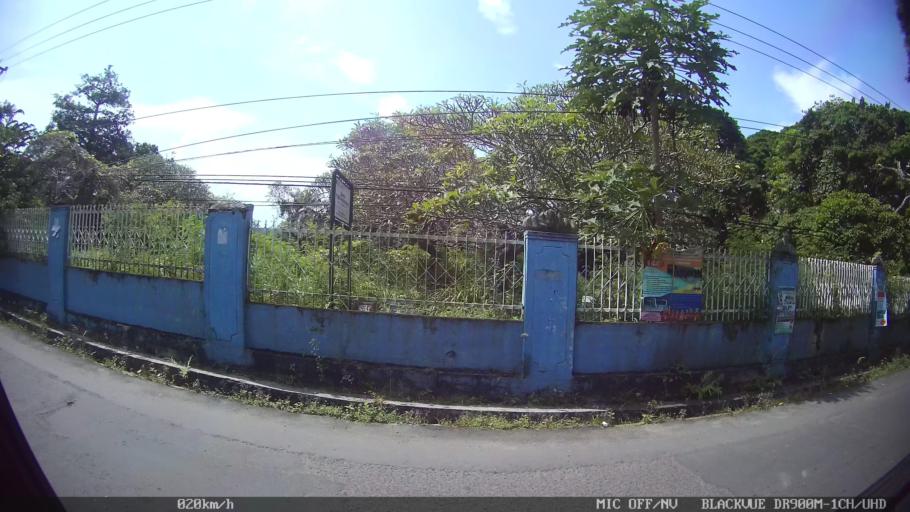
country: ID
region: Lampung
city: Bandarlampung
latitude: -5.4144
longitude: 105.2610
